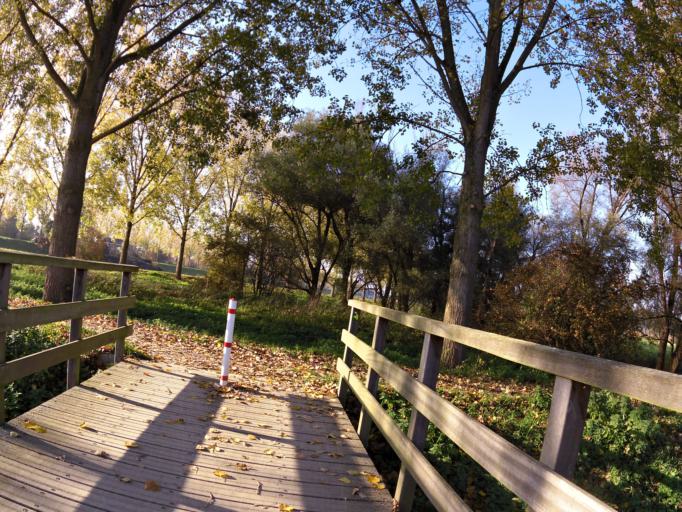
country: NL
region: Gelderland
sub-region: Gemeente Maasdriel
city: Hedel
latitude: 51.7233
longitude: 5.2735
